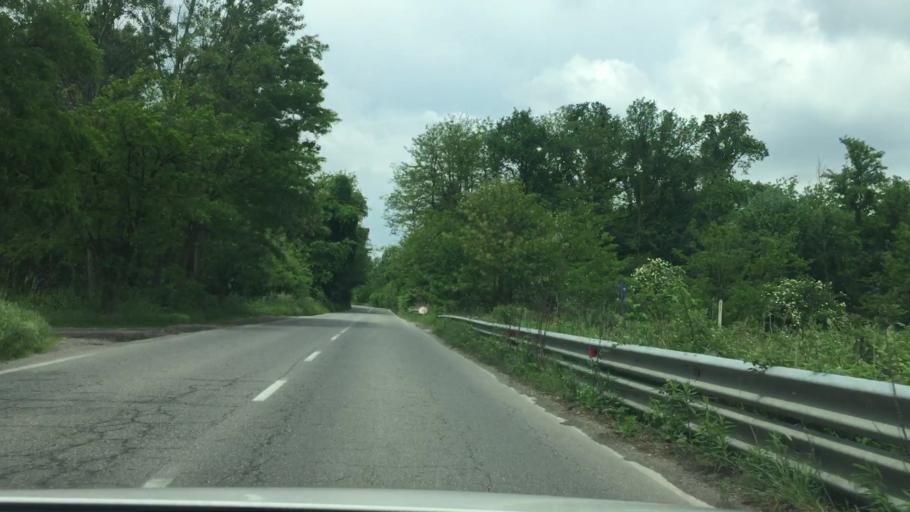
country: IT
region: Lombardy
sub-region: Provincia di Varese
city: Lonate Pozzolo
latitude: 45.5689
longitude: 8.7458
